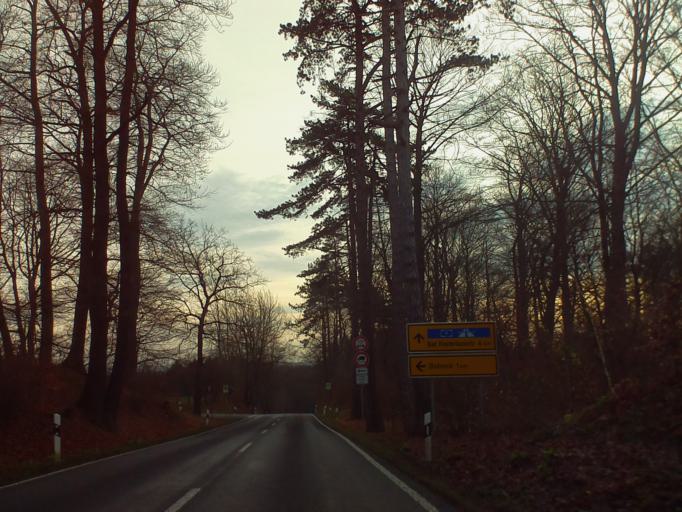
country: DE
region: Thuringia
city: Bobeck
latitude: 50.8956
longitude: 11.7902
